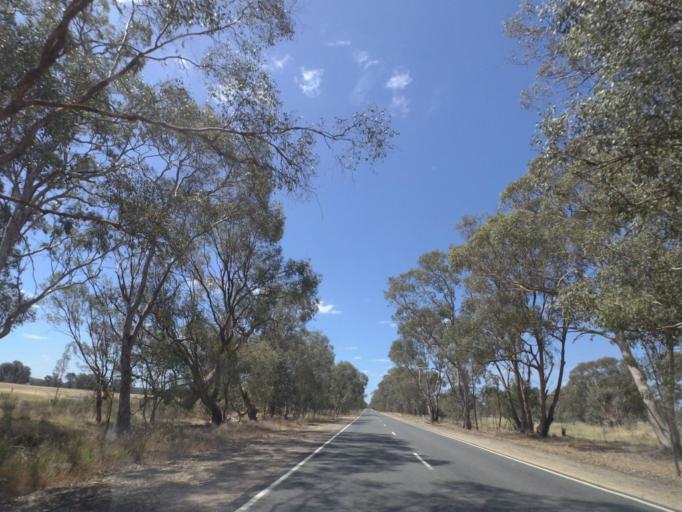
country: AU
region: Victoria
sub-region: Wangaratta
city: Wangaratta
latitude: -36.4341
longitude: 146.2510
